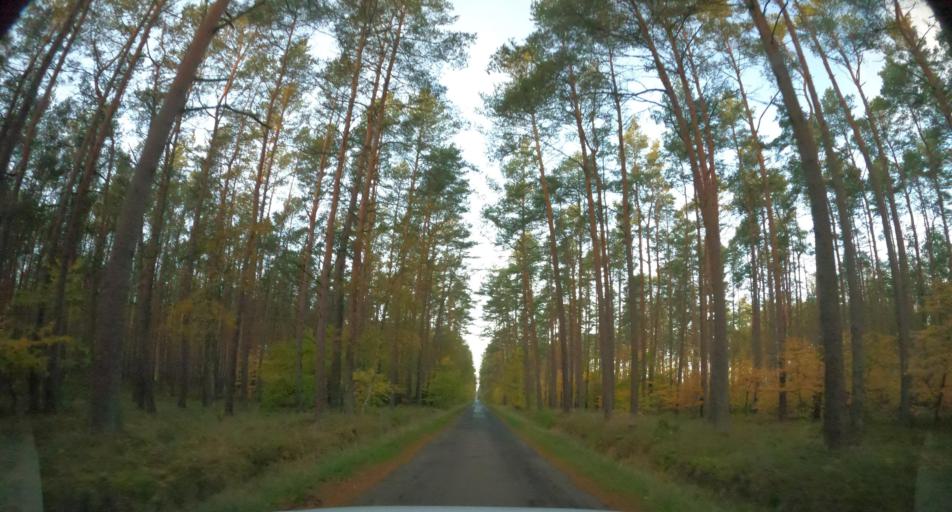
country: PL
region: West Pomeranian Voivodeship
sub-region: Powiat policki
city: Nowe Warpno
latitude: 53.6420
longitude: 14.3903
